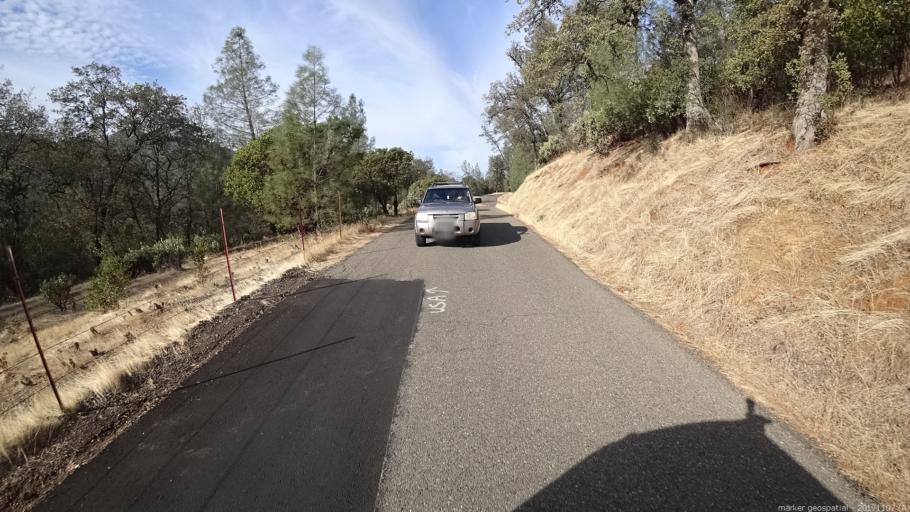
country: US
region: California
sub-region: Shasta County
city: Shasta
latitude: 40.5259
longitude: -122.5306
